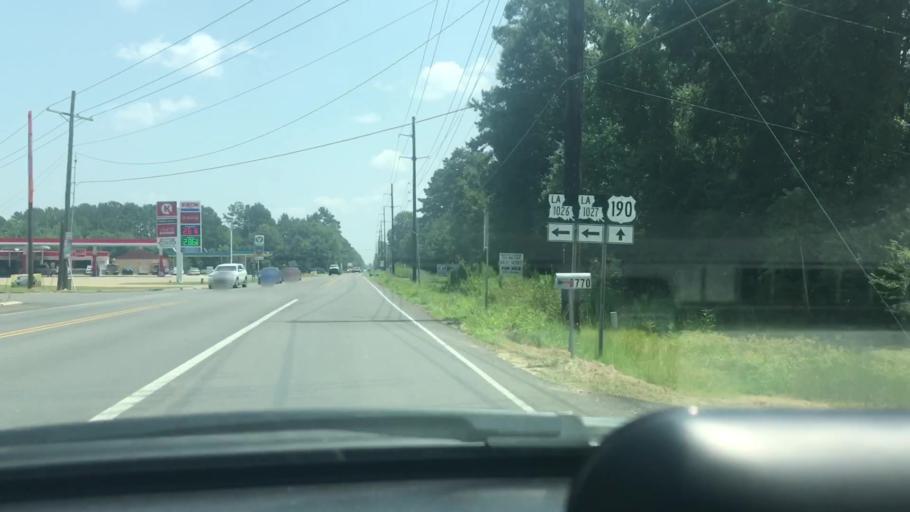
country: US
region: Louisiana
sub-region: Livingston Parish
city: Walker
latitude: 30.4836
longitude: -90.9064
